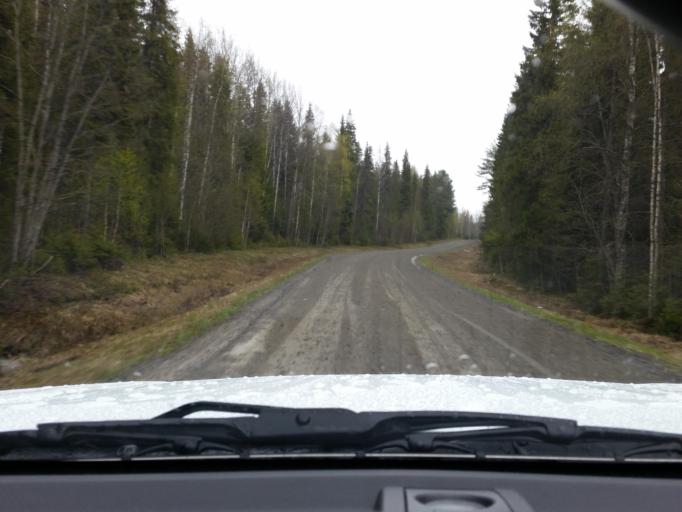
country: SE
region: Norrbotten
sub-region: Pitea Kommun
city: Norrfjarden
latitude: 65.6005
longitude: 21.4329
